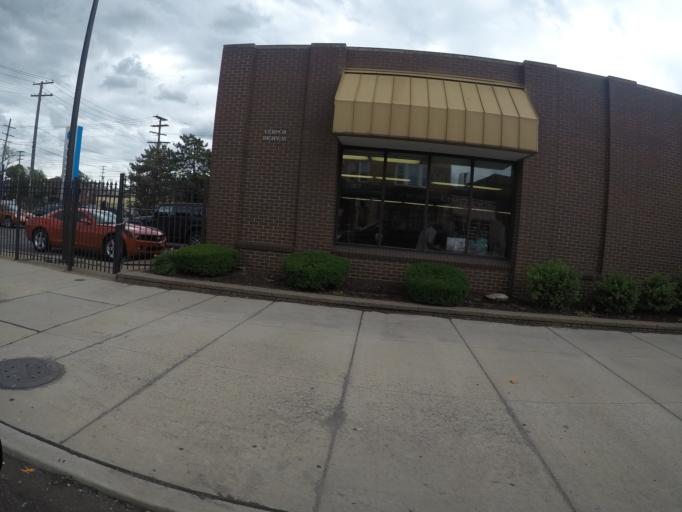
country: US
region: Michigan
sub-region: Wayne County
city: River Rouge
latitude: 42.3113
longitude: -83.1276
